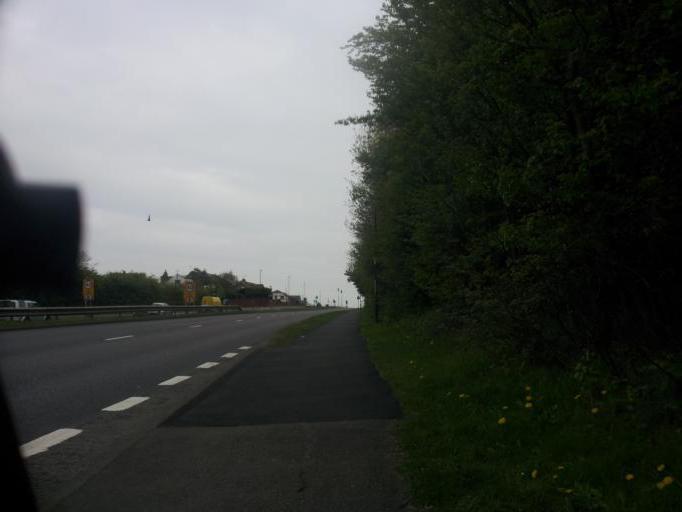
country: GB
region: England
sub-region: Medway
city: Rochester
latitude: 51.4168
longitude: 0.5244
